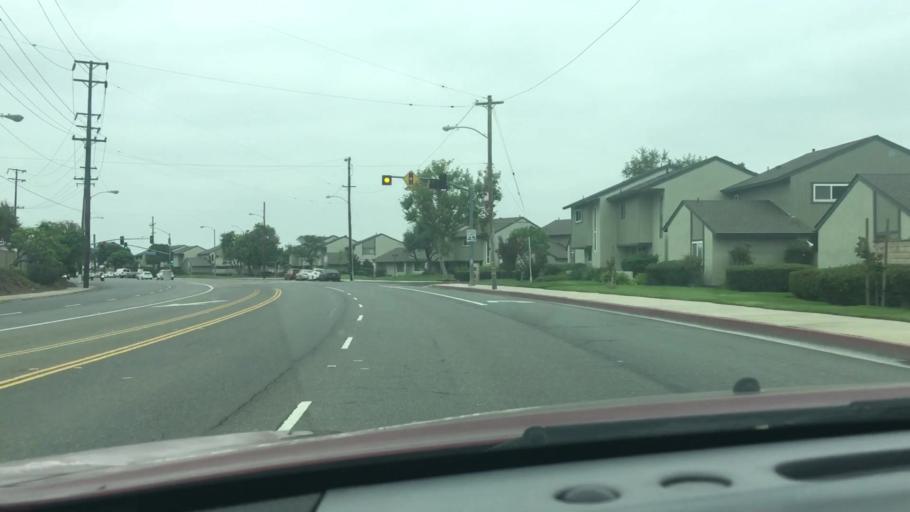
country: US
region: California
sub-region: Orange County
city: Buena Park
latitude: 33.8800
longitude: -117.9925
